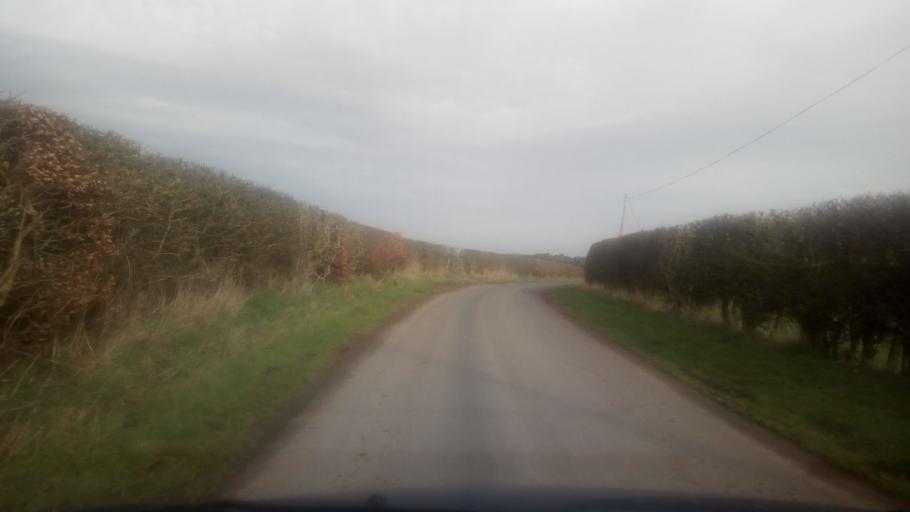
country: GB
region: Scotland
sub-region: The Scottish Borders
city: Hawick
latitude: 55.4347
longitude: -2.6959
